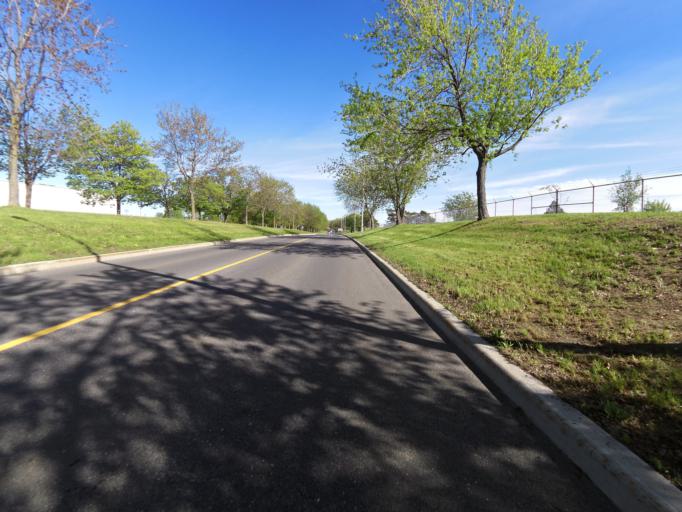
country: CA
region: Ontario
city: Ottawa
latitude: 45.3328
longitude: -75.6788
